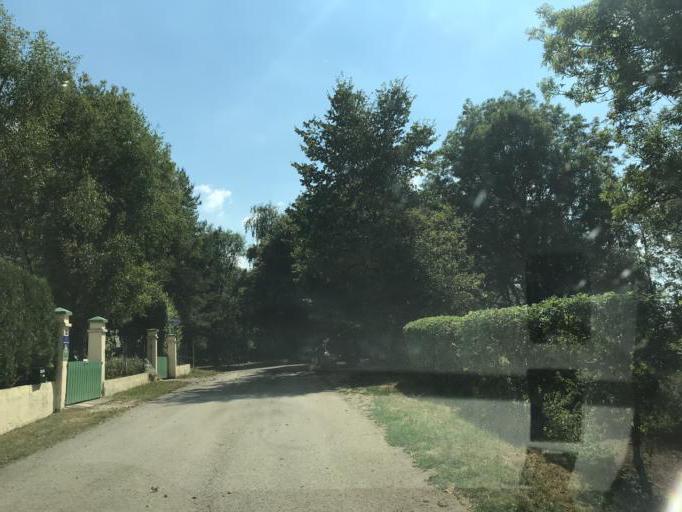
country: FR
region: Franche-Comte
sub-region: Departement du Jura
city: Clairvaux-les-Lacs
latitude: 46.5903
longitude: 5.7351
